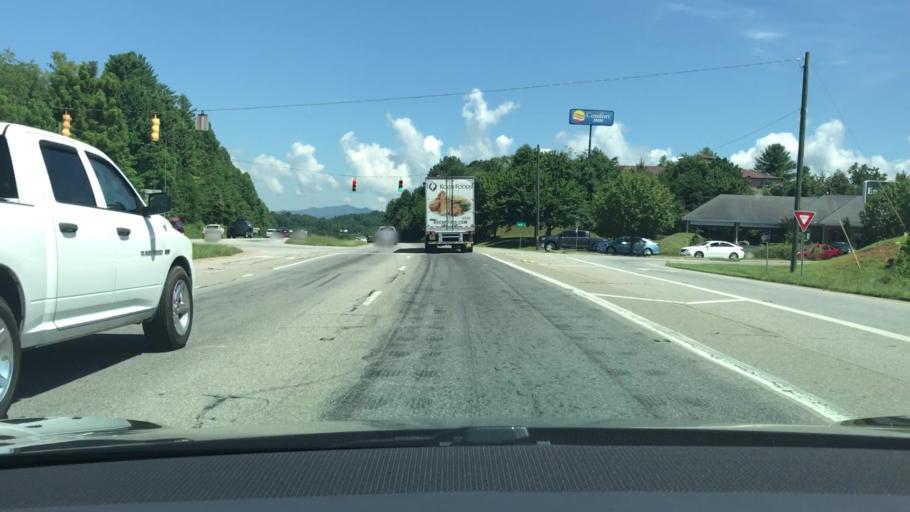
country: US
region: North Carolina
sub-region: Macon County
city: Franklin
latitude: 35.1825
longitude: -83.3569
